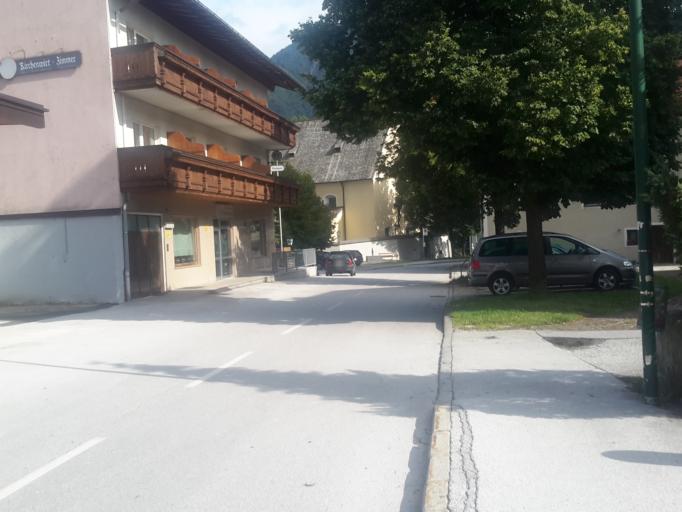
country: AT
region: Tyrol
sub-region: Politischer Bezirk Kufstein
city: Kufstein
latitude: 47.5861
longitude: 12.1630
